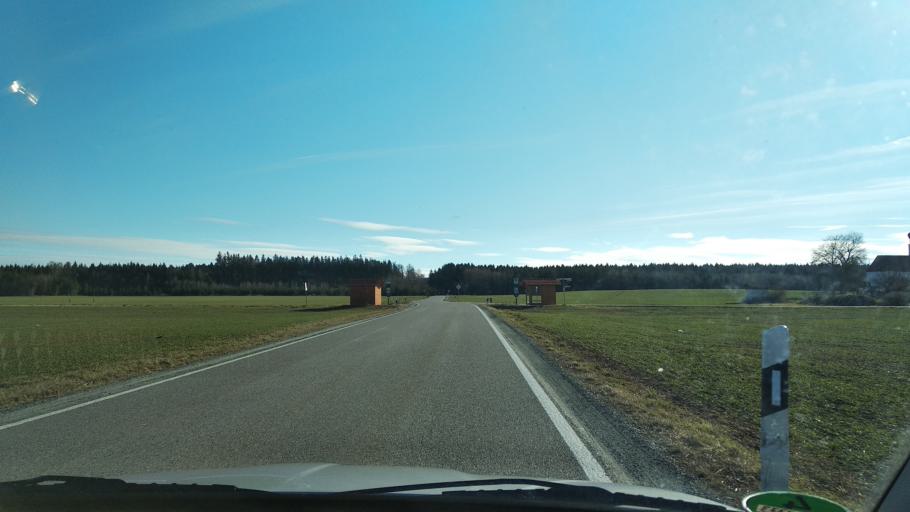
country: DE
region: Bavaria
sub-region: Upper Bavaria
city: Oberpframmern
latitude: 48.0485
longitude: 11.8164
